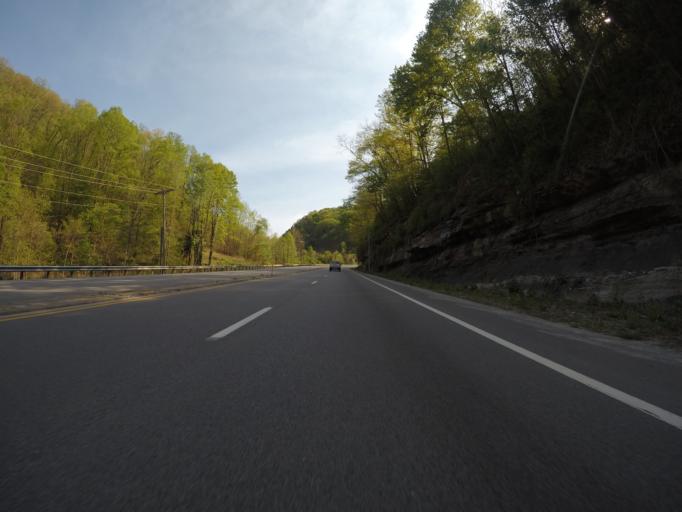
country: US
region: West Virginia
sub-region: Kanawha County
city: Charleston
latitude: 38.3540
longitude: -81.5979
